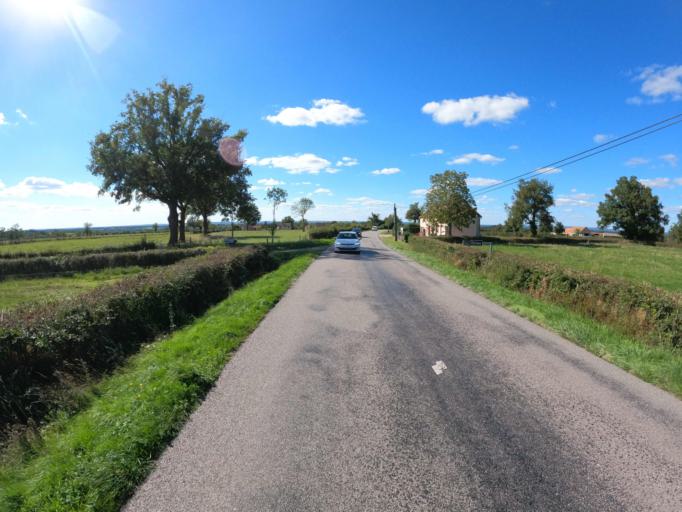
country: FR
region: Auvergne
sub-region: Departement de l'Allier
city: Buxieres-les-Mines
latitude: 46.4033
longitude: 2.9183
